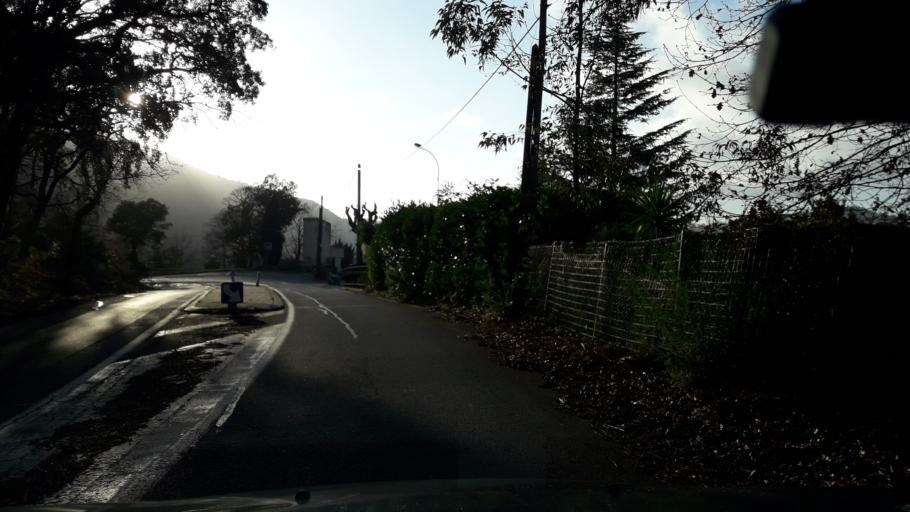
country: FR
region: Provence-Alpes-Cote d'Azur
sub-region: Departement du Var
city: Tanneron
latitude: 43.5184
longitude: 6.8378
